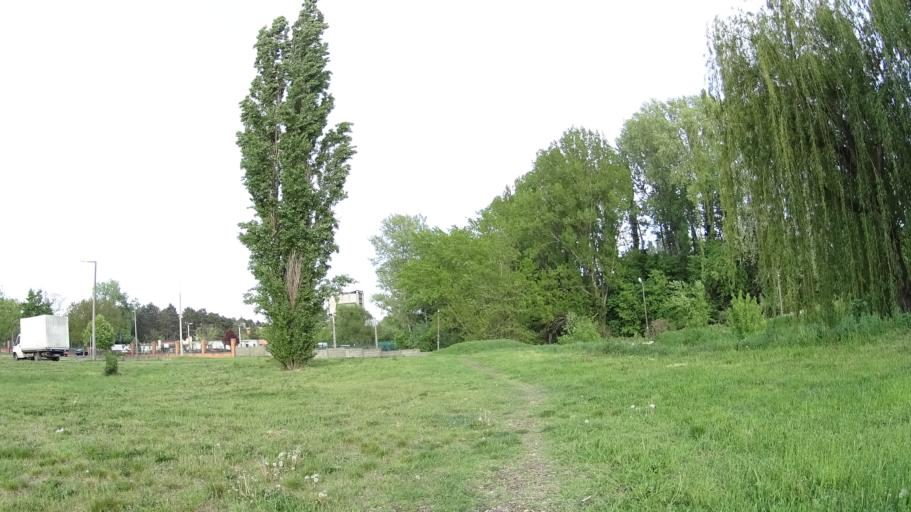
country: HU
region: Pest
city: Vac
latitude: 47.7687
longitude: 19.1448
